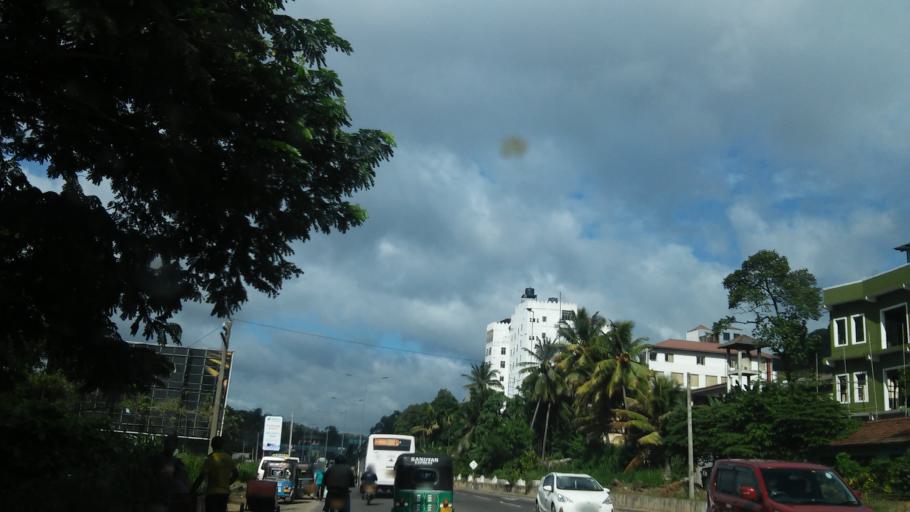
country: LK
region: Central
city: Kandy
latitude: 7.2783
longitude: 80.6178
